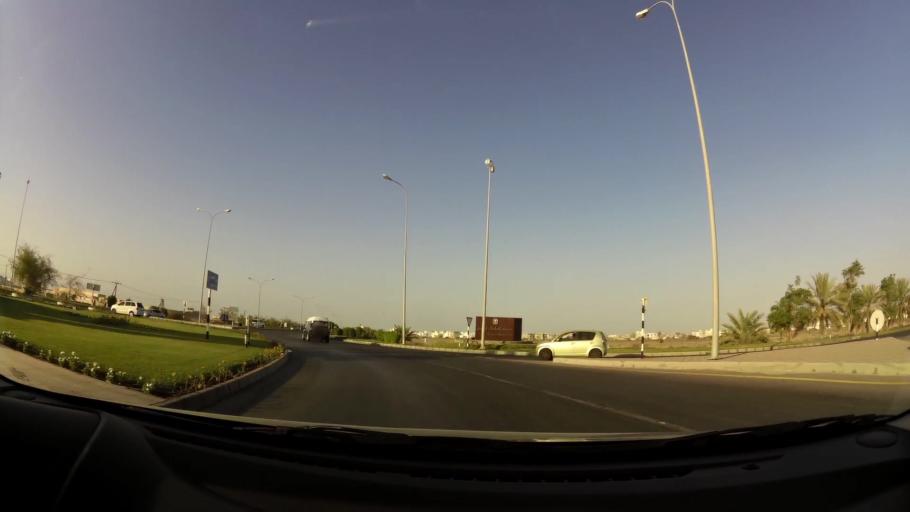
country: OM
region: Muhafazat Masqat
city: As Sib al Jadidah
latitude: 23.6062
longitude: 58.1652
